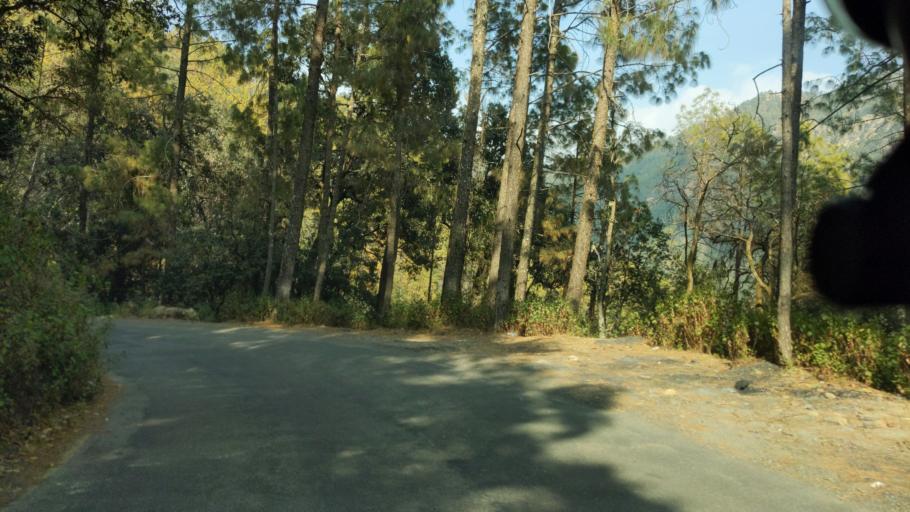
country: IN
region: Uttarakhand
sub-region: Naini Tal
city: Bhowali
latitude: 29.4044
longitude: 79.5378
